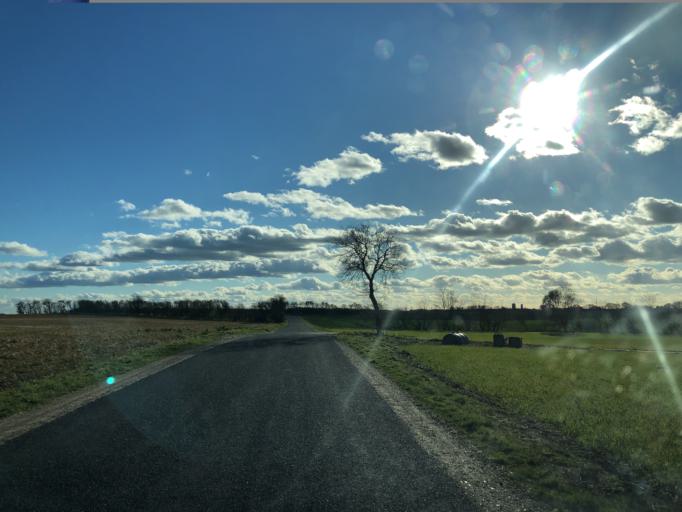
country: DK
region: Central Jutland
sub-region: Silkeborg Kommune
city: Kjellerup
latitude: 56.3403
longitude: 9.5071
